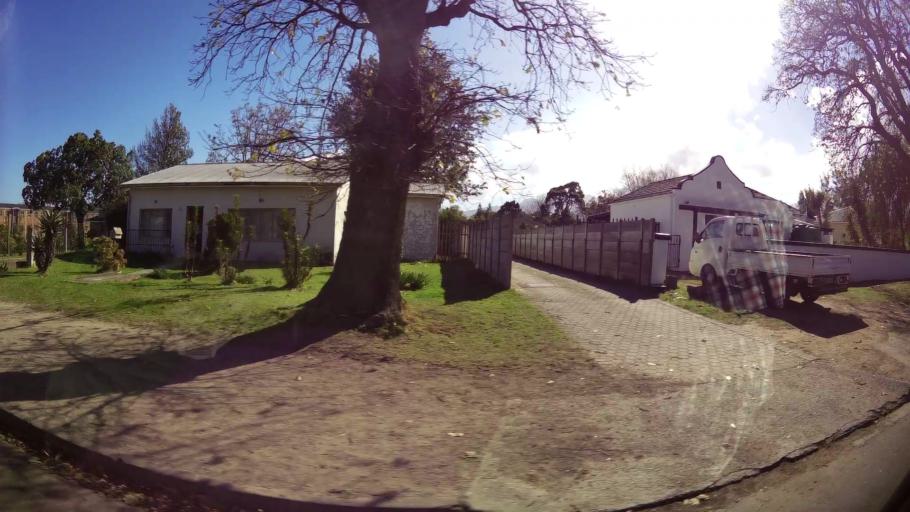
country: ZA
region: Western Cape
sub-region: Eden District Municipality
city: George
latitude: -33.9699
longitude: 22.4524
